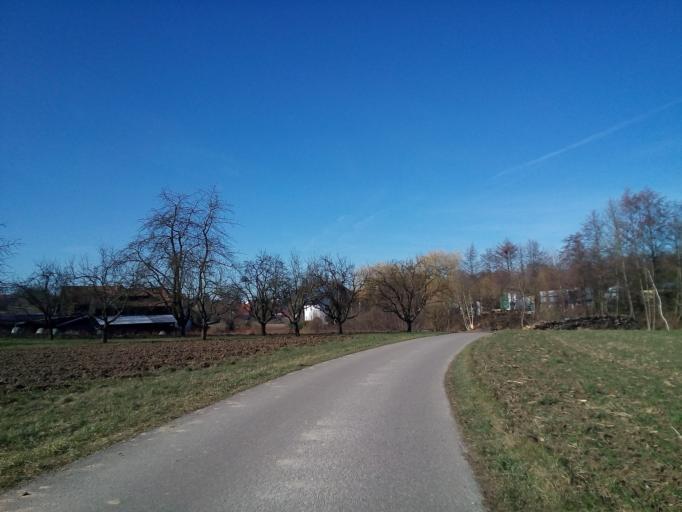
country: DE
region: Baden-Wuerttemberg
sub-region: Freiburg Region
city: Achern
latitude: 48.6124
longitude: 8.0630
